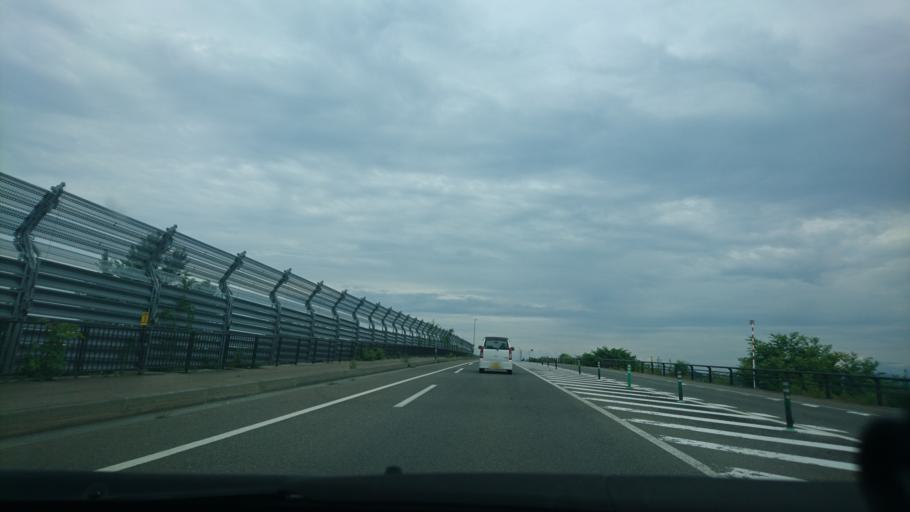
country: JP
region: Akita
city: Omagari
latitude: 39.4896
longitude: 140.4520
